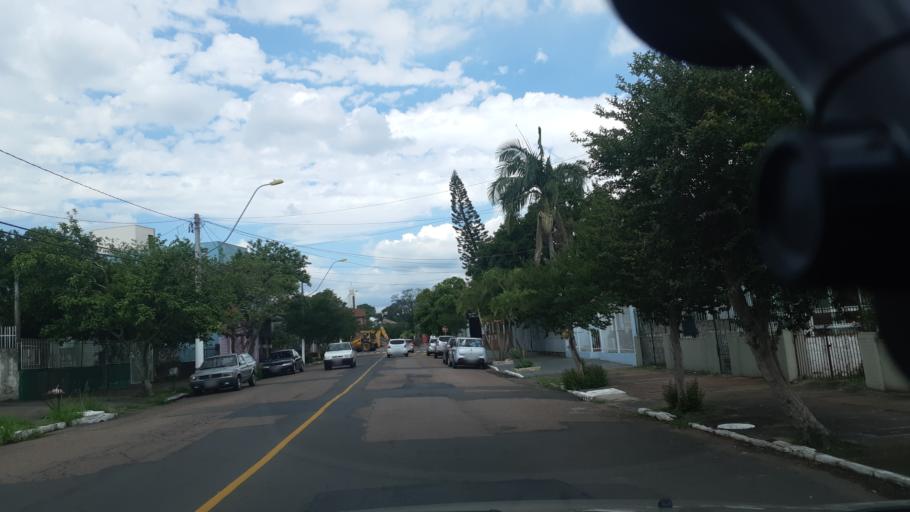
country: BR
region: Rio Grande do Sul
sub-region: Esteio
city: Esteio
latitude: -29.8502
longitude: -51.1693
